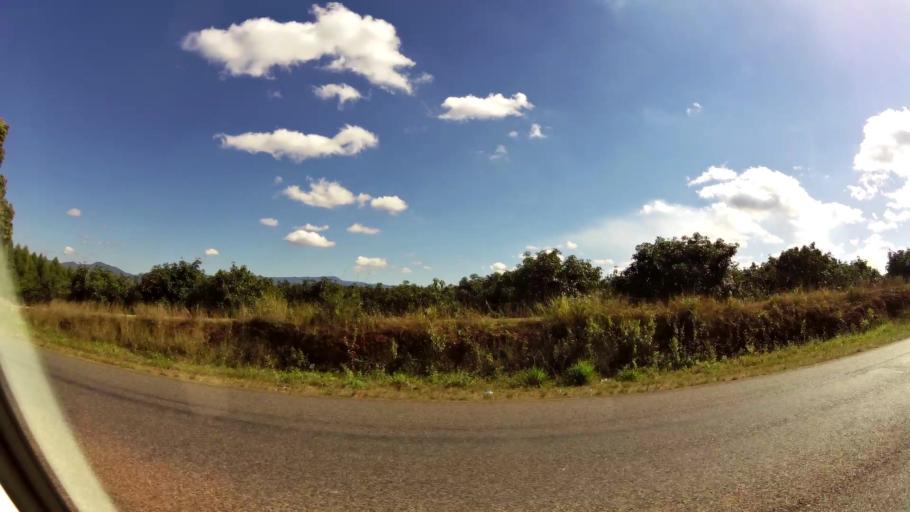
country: ZA
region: Limpopo
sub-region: Mopani District Municipality
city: Tzaneen
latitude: -23.8071
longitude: 30.1774
